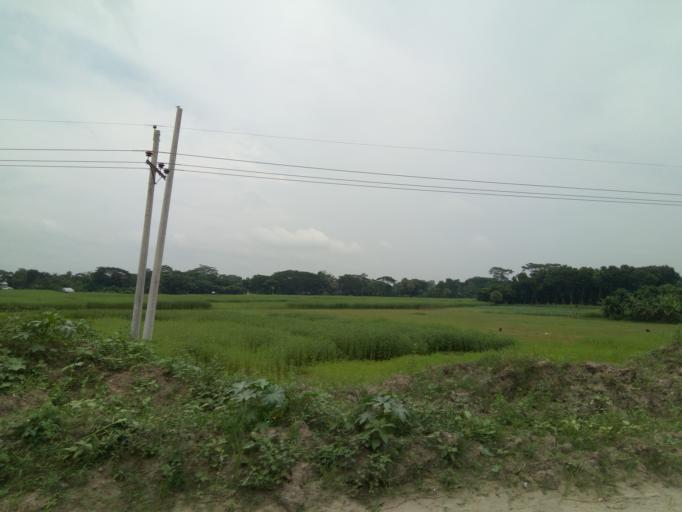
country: BD
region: Dhaka
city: Char Bhadrasan
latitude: 23.3769
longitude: 90.0179
